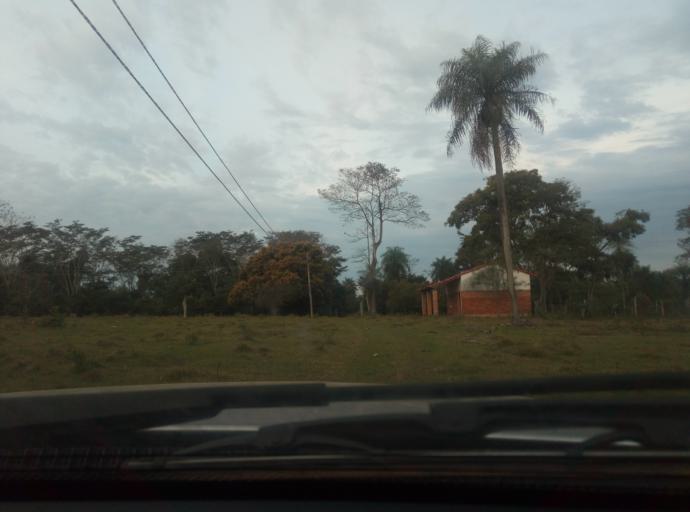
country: PY
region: Caaguazu
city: Carayao
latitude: -25.1464
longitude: -56.3934
